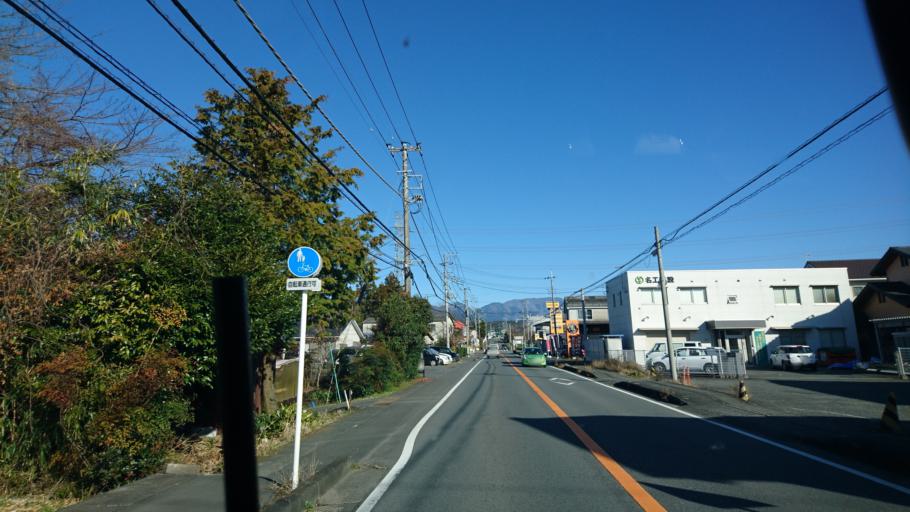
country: JP
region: Shizuoka
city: Fujinomiya
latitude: 35.2530
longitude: 138.6090
